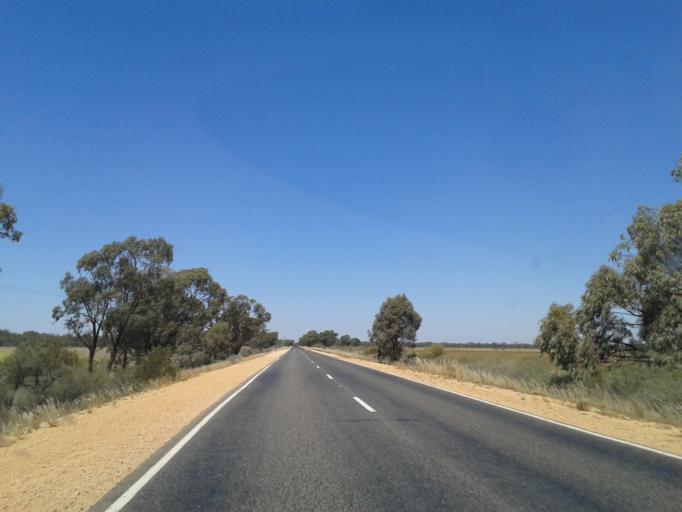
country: AU
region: Victoria
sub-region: Swan Hill
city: Swan Hill
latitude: -34.7088
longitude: 143.0883
